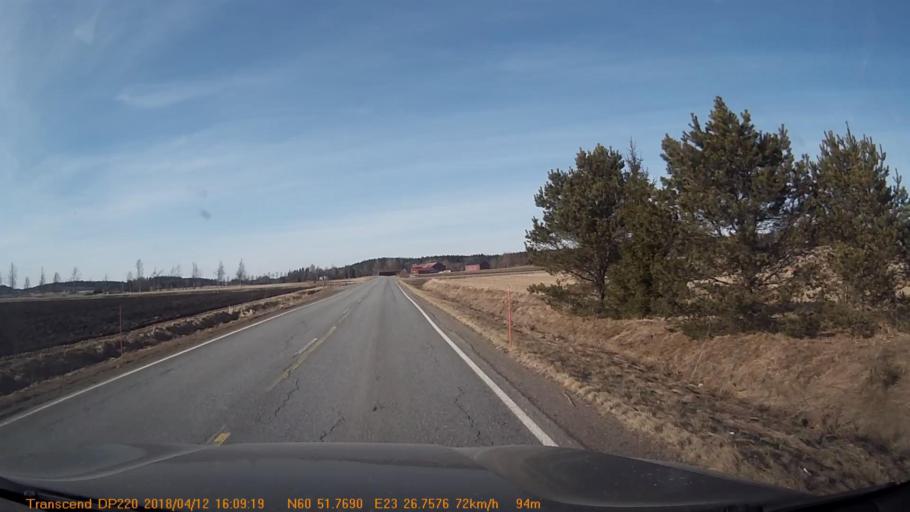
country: FI
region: Haeme
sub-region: Forssa
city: Jokioinen
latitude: 60.8627
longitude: 23.4460
